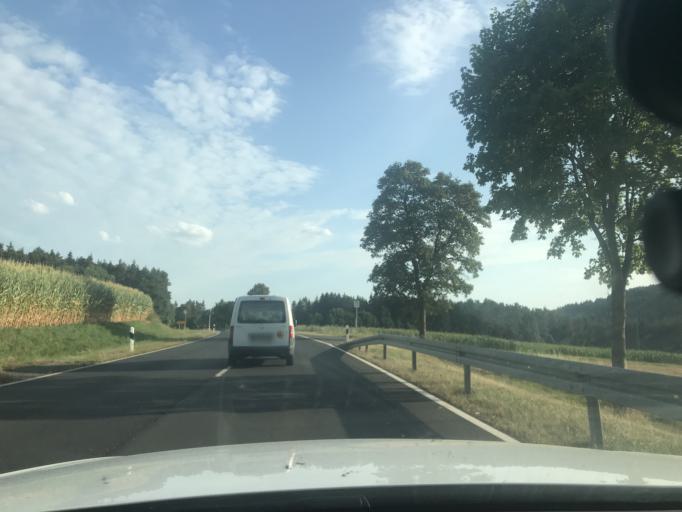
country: DE
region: Bavaria
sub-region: Upper Franconia
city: Pegnitz
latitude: 49.7969
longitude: 11.5791
